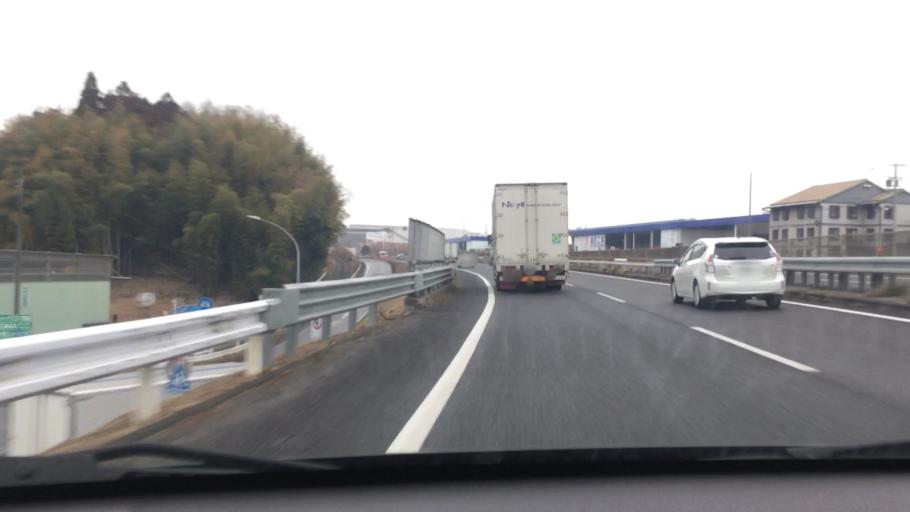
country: JP
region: Mie
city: Ueno-ebisumachi
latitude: 34.7060
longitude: 136.0755
